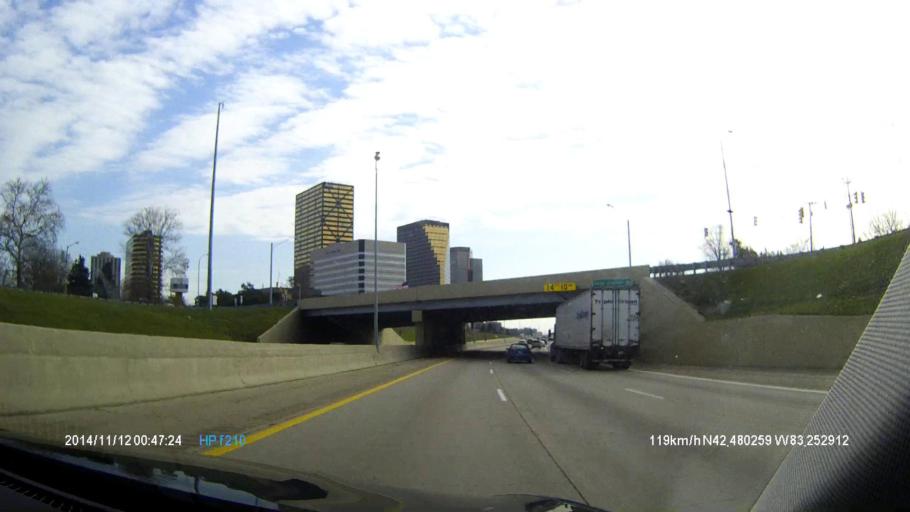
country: US
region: Michigan
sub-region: Oakland County
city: Southfield
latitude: 42.4802
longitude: -83.2527
